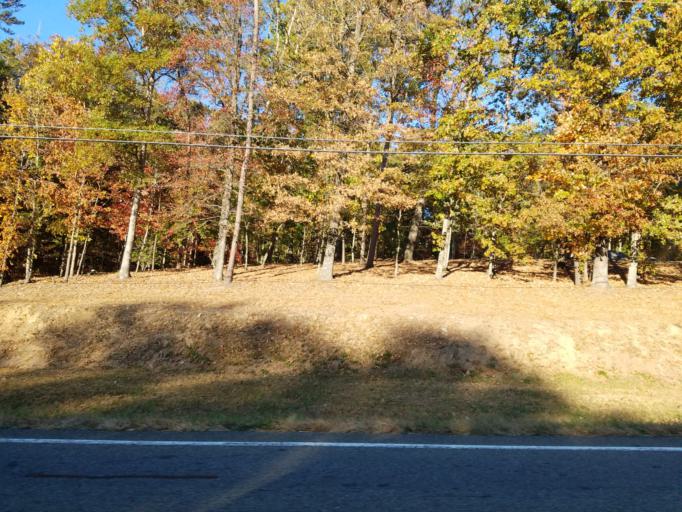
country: US
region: Georgia
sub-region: Gilmer County
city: Ellijay
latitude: 34.6523
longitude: -84.4346
